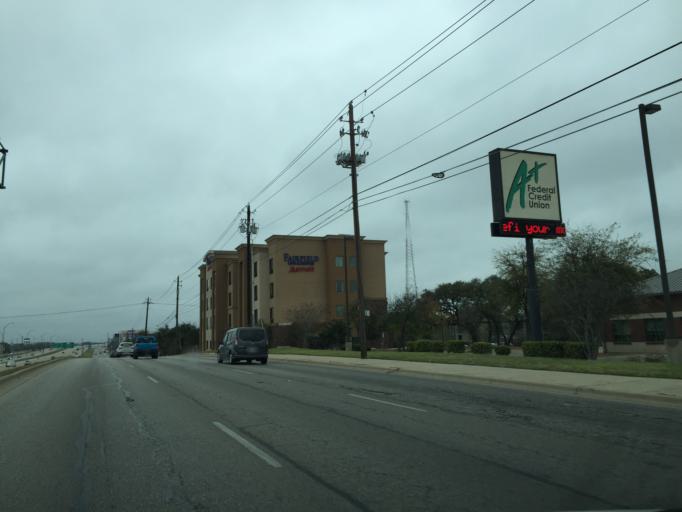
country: US
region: Texas
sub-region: Williamson County
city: Jollyville
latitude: 30.4399
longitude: -97.7792
